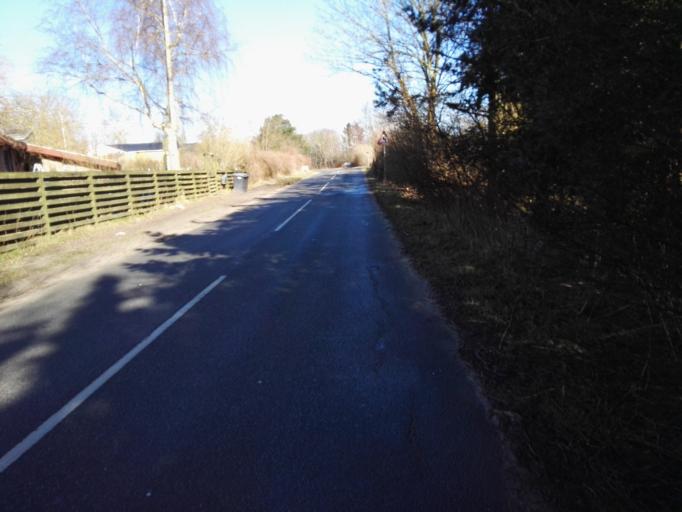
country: DK
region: Zealand
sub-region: Lejre Kommune
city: Ejby
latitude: 55.7644
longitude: 11.8192
